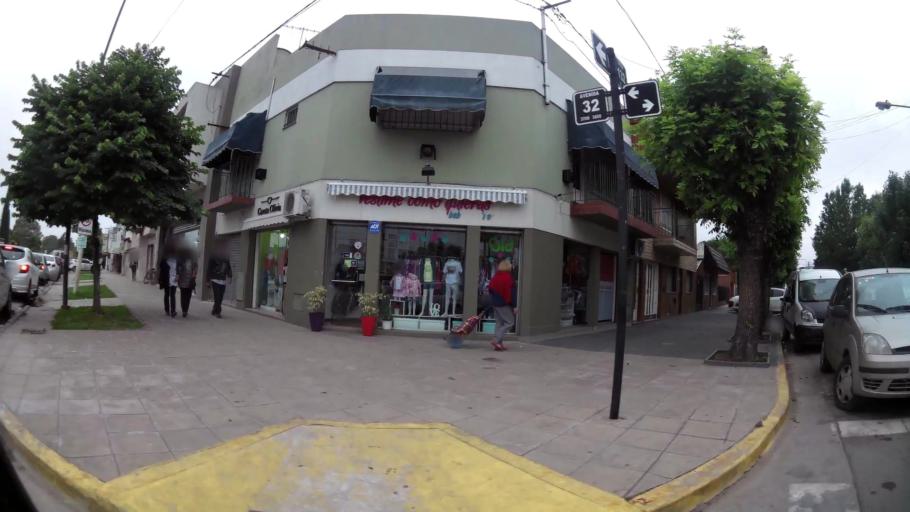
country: AR
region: Buenos Aires
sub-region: Partido de La Plata
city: La Plata
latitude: -34.9245
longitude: -57.9950
